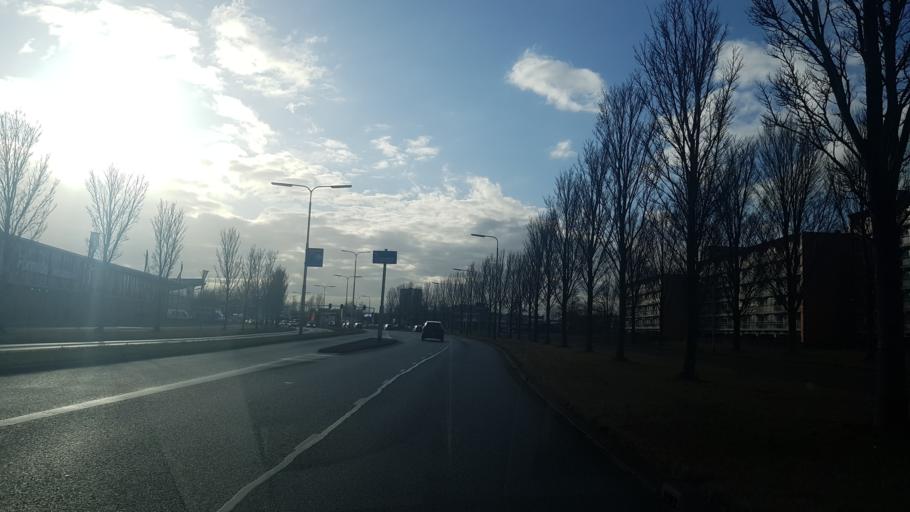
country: NL
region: Friesland
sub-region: Gemeente Leeuwarden
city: Leeuwarden
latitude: 53.2138
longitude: 5.8172
